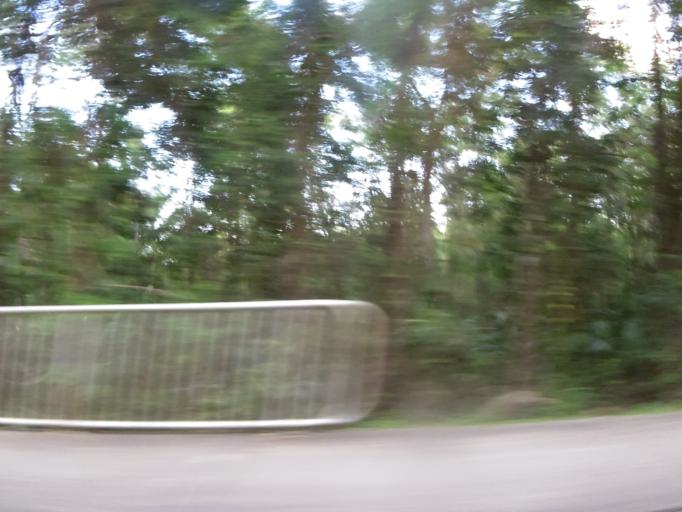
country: US
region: Florida
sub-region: Saint Johns County
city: Fruit Cove
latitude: 30.1163
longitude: -81.5757
